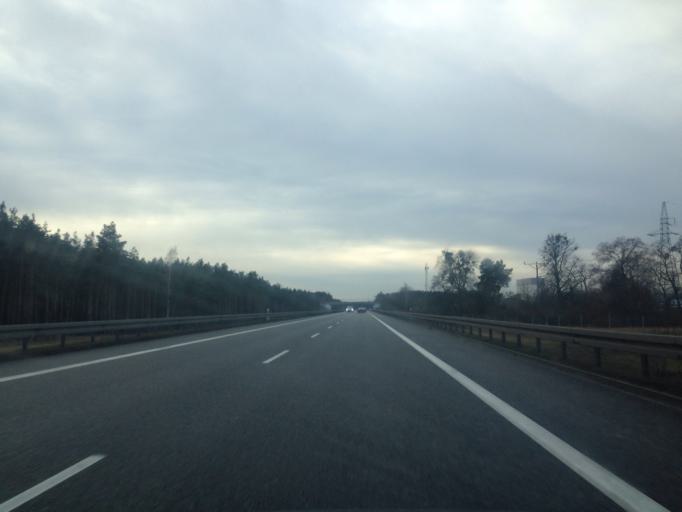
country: PL
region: Kujawsko-Pomorskie
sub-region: Torun
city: Torun
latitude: 52.9791
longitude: 18.5738
